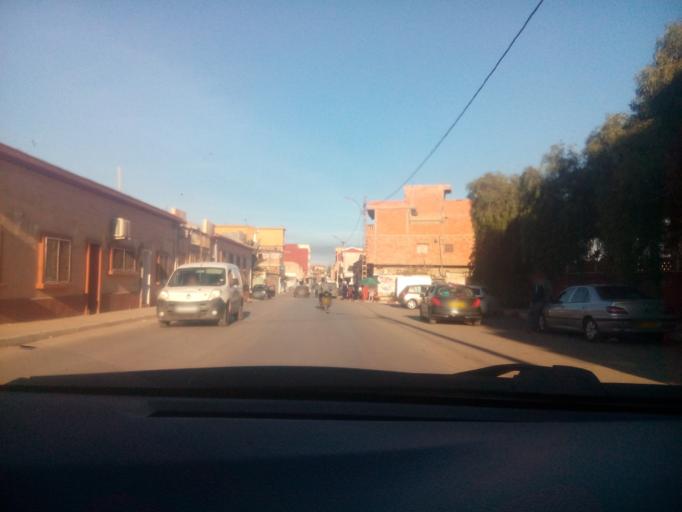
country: DZ
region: Oran
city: Bir el Djir
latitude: 35.7781
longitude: -0.4309
